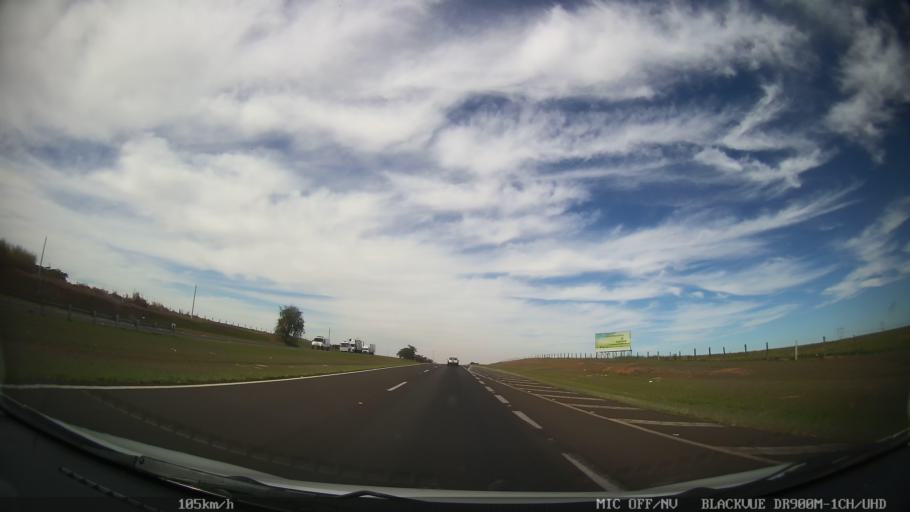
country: BR
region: Sao Paulo
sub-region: Matao
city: Matao
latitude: -21.5586
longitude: -48.4782
